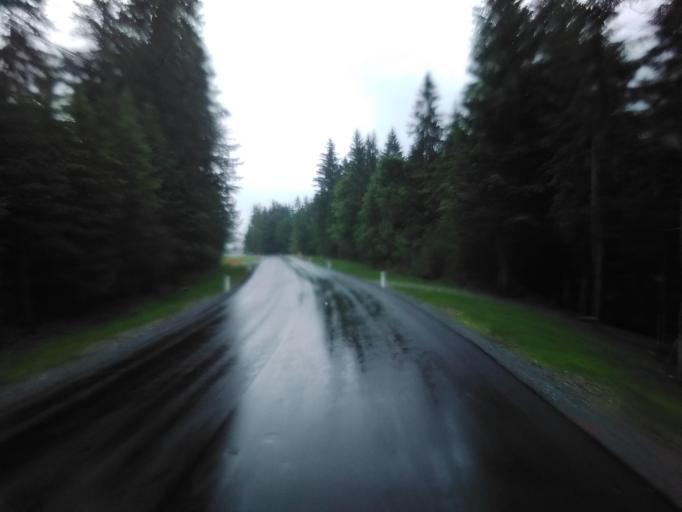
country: AT
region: Tyrol
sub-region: Politischer Bezirk Kitzbuhel
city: Schwendt
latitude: 47.5951
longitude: 12.3817
